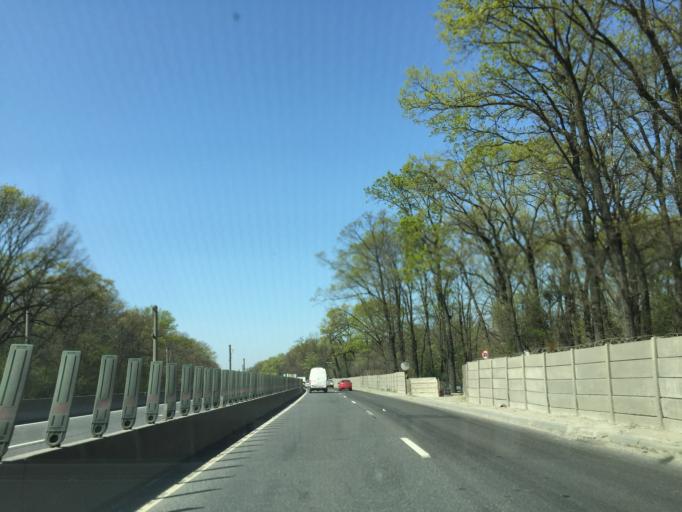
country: RO
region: Ilfov
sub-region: Comuna Tunari
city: Tunari
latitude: 44.5390
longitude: 26.1222
